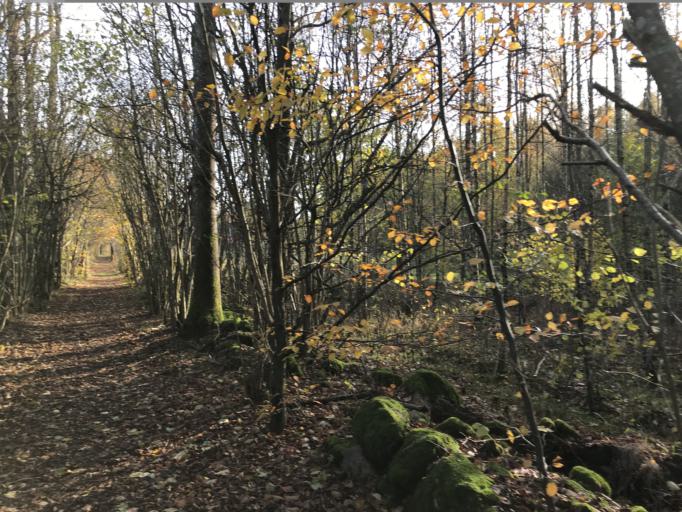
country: SE
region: Skane
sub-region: Svalovs Kommun
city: Kagerod
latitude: 56.0256
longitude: 13.1055
